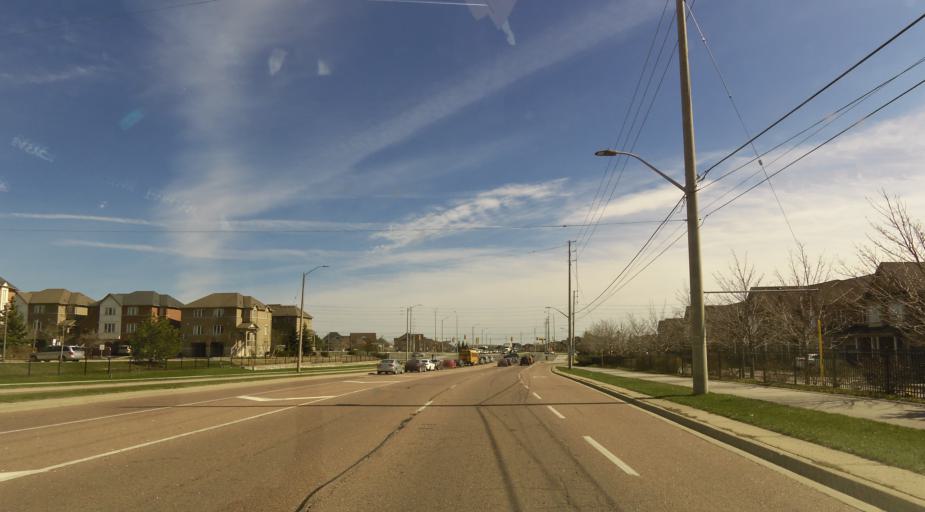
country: CA
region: Ontario
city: Brampton
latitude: 43.6342
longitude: -79.7233
